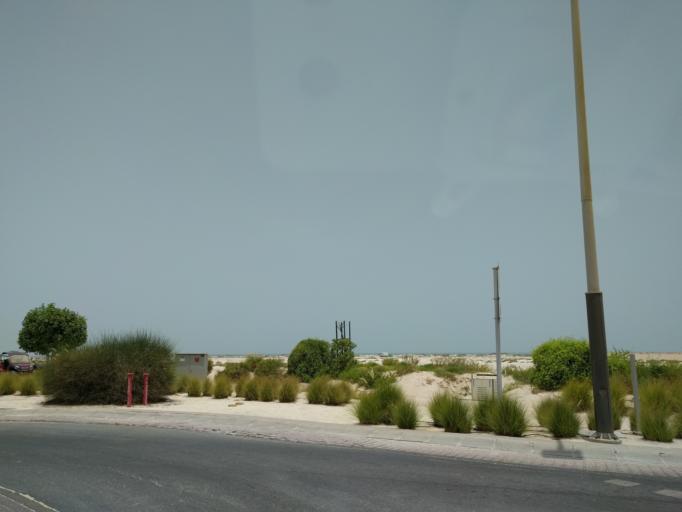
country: AE
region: Abu Dhabi
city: Abu Dhabi
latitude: 24.5539
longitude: 54.4485
